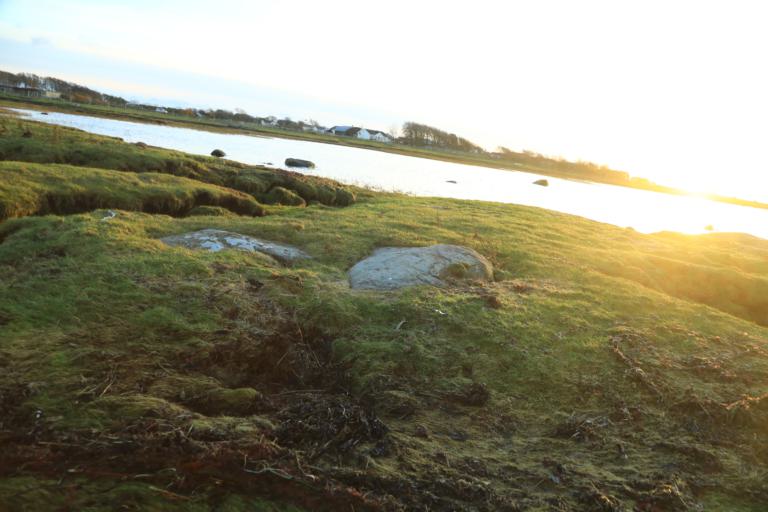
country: SE
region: Halland
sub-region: Varbergs Kommun
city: Traslovslage
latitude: 57.0743
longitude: 12.2606
